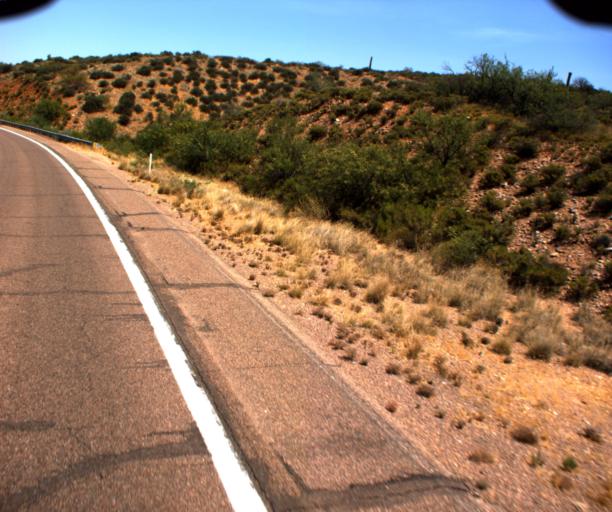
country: US
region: Arizona
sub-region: Gila County
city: Tonto Basin
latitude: 33.7368
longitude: -111.2193
